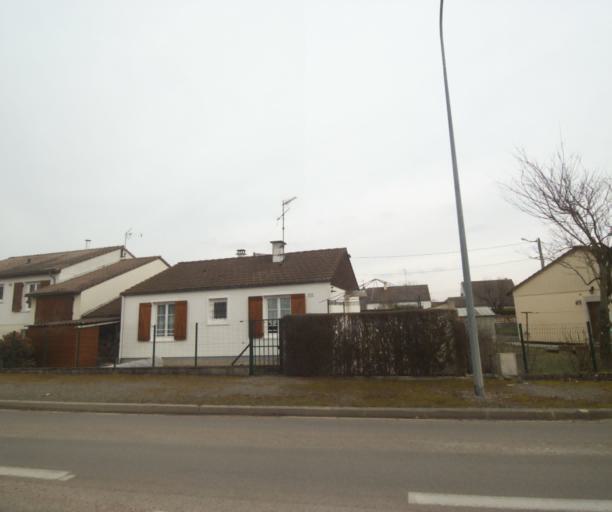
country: FR
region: Champagne-Ardenne
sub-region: Departement de la Haute-Marne
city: Villiers-en-Lieu
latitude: 48.6686
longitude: 4.8944
